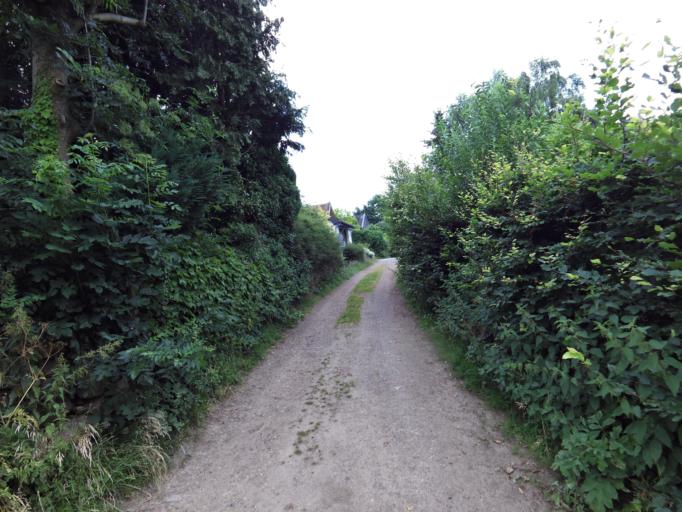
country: BE
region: Wallonia
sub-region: Province de Liege
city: Plombieres
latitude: 50.7873
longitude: 5.9450
